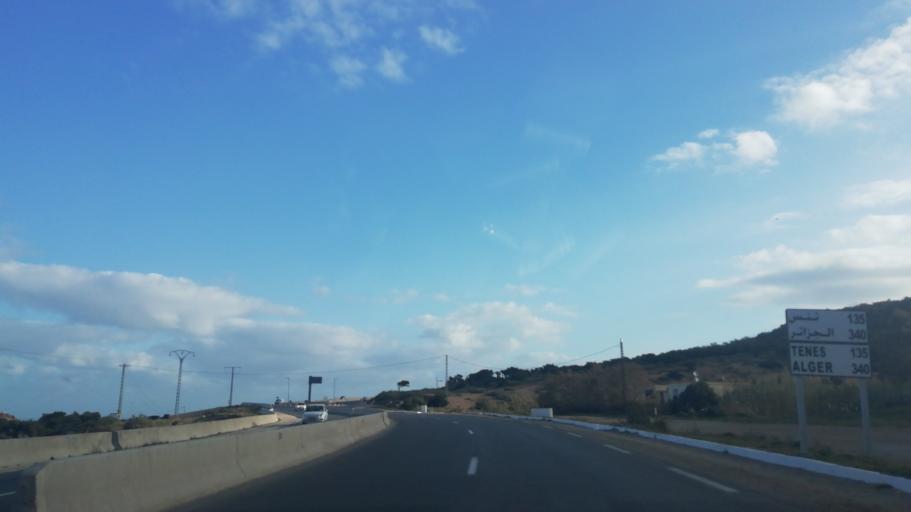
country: DZ
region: Mostaganem
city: Mostaganem
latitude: 36.1026
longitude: 0.2140
